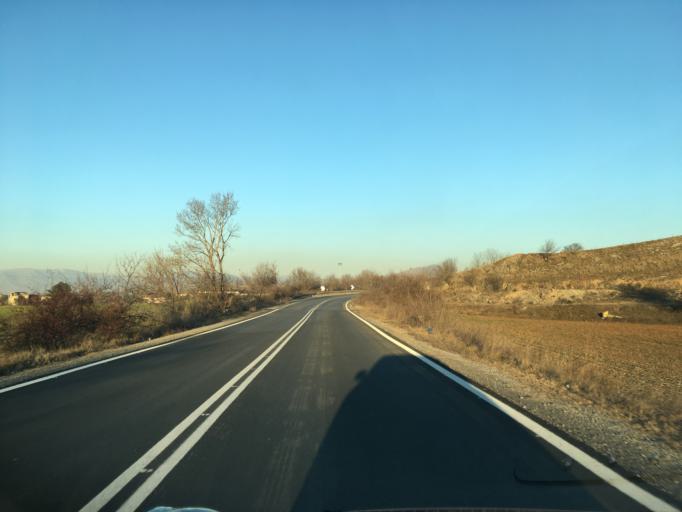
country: GR
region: West Macedonia
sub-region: Nomos Kozanis
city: Koila
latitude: 40.3251
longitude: 21.7787
